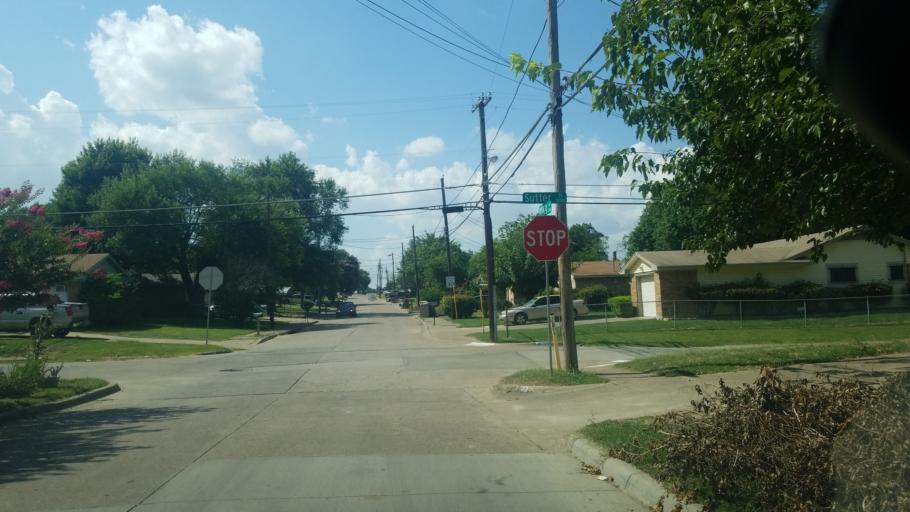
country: US
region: Texas
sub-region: Dallas County
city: Dallas
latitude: 32.7164
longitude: -96.7941
